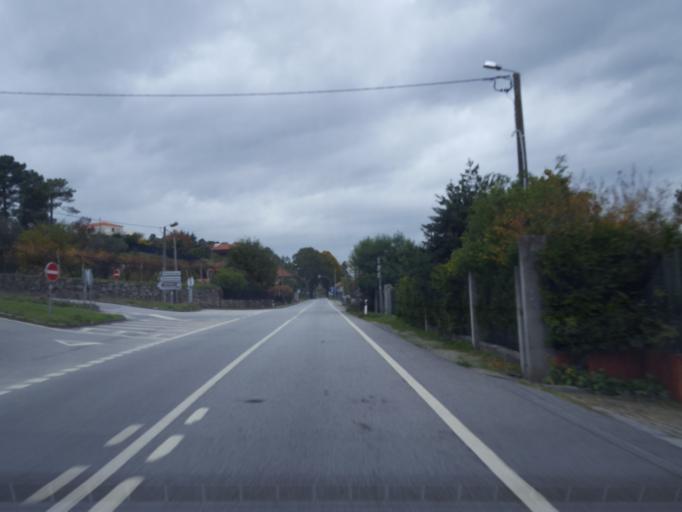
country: PT
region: Porto
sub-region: Marco de Canaveses
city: Marco de Canavezes
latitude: 41.1581
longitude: -8.1443
